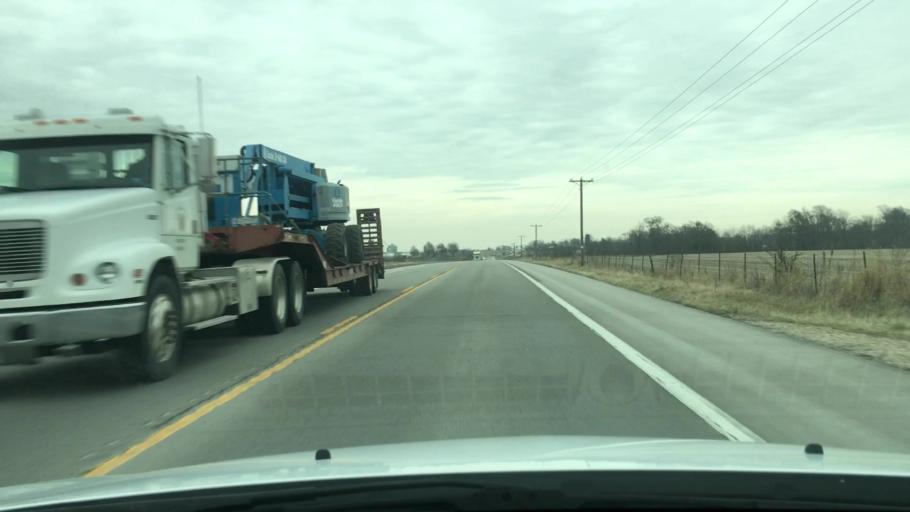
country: US
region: Missouri
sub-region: Audrain County
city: Mexico
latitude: 39.1644
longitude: -91.7137
